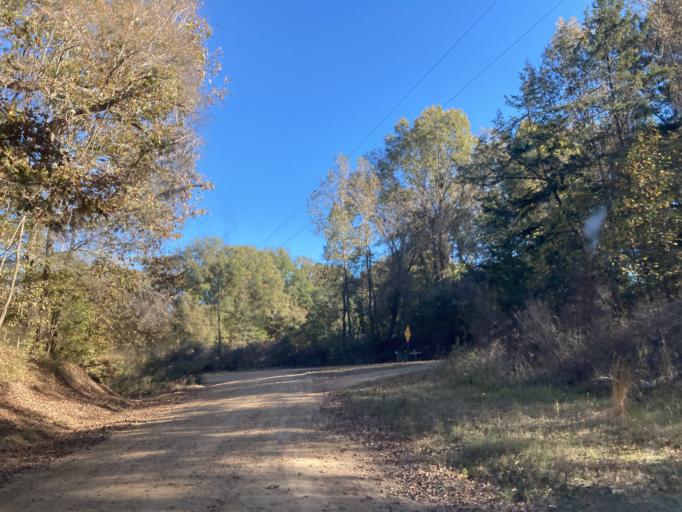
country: US
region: Mississippi
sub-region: Yazoo County
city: Yazoo City
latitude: 32.7439
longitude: -90.4330
